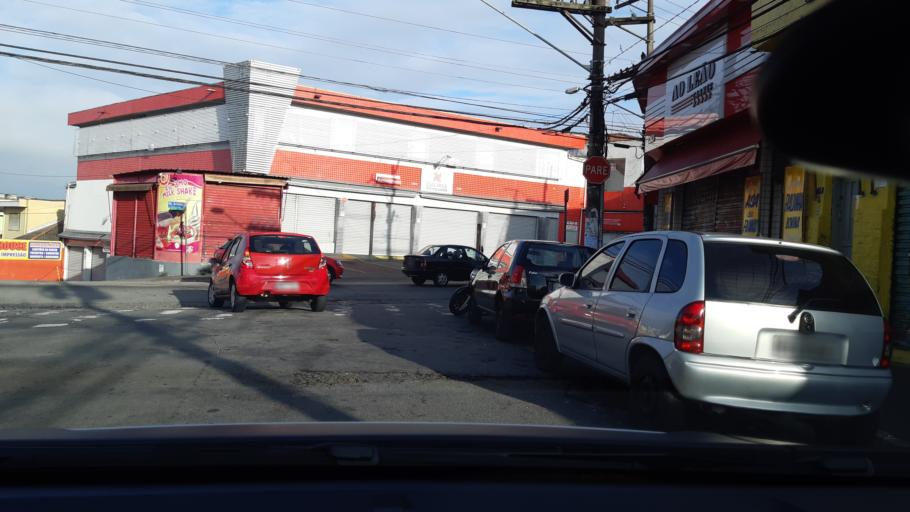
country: BR
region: Sao Paulo
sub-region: Sao Caetano Do Sul
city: Sao Caetano do Sul
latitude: -23.6322
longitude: -46.6045
